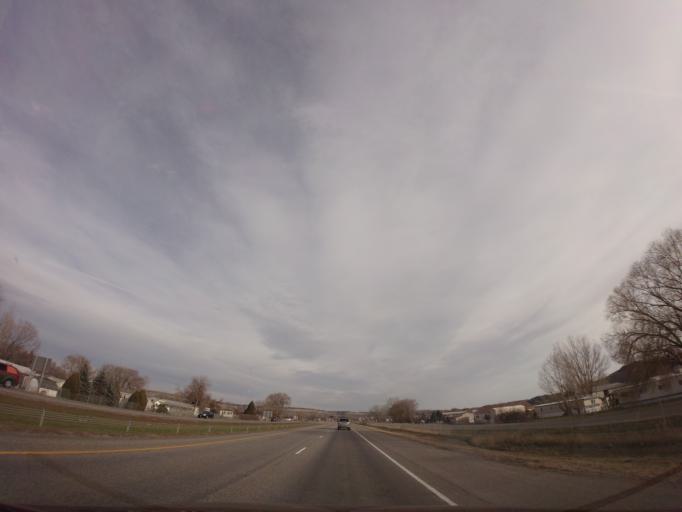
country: US
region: Montana
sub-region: Yellowstone County
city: Billings
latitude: 45.7521
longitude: -108.5219
